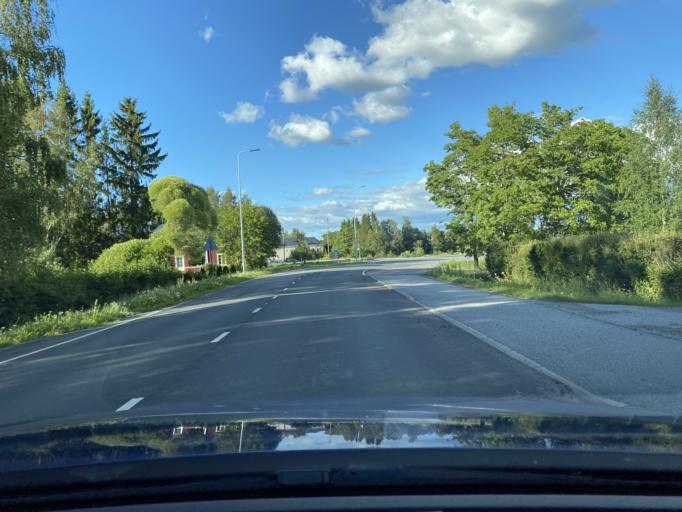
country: FI
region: Ostrobothnia
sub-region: Kyroenmaa
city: Laihia
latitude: 62.9847
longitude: 22.0017
